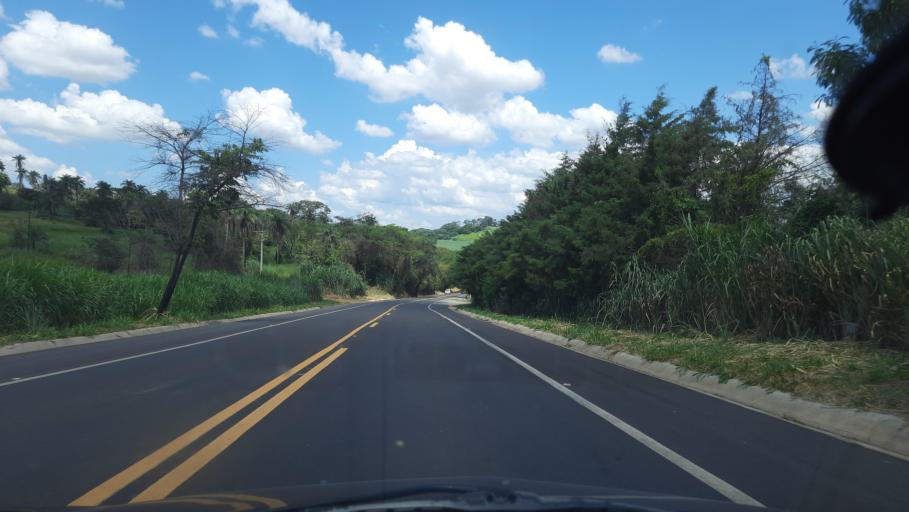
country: BR
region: Sao Paulo
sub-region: Sao Jose Do Rio Pardo
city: Sao Jose do Rio Pardo
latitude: -21.5941
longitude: -46.9888
